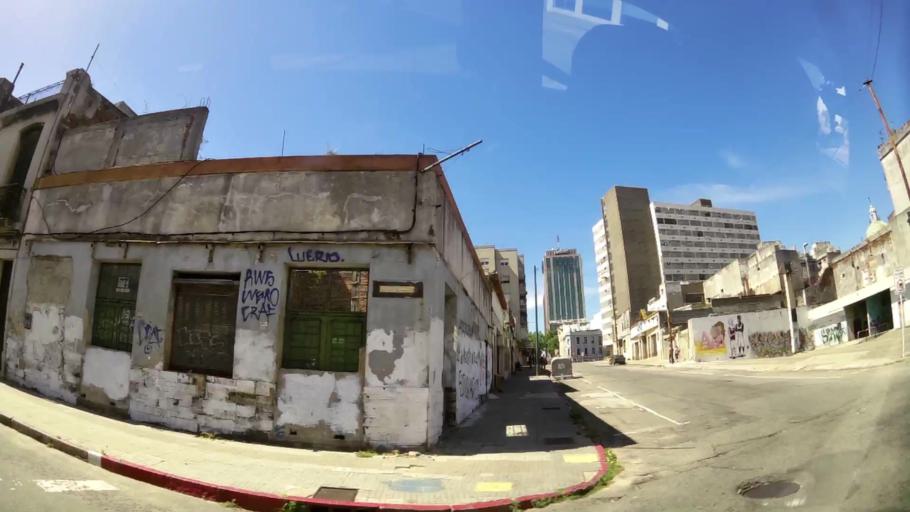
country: UY
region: Montevideo
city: Montevideo
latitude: -34.9005
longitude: -56.1952
